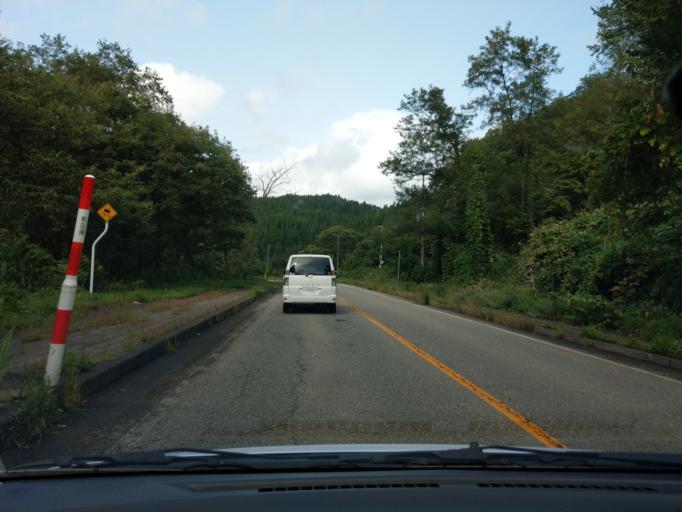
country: JP
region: Akita
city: Omagari
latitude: 39.4337
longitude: 140.3768
